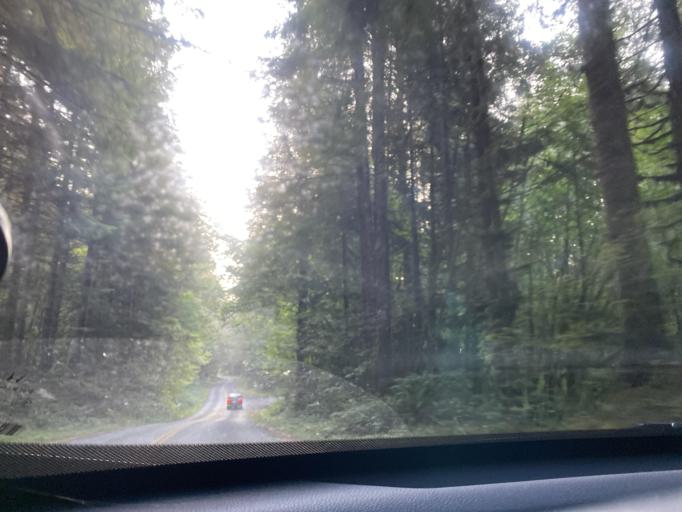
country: US
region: Washington
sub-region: Clallam County
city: Forks
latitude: 47.8164
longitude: -124.0529
